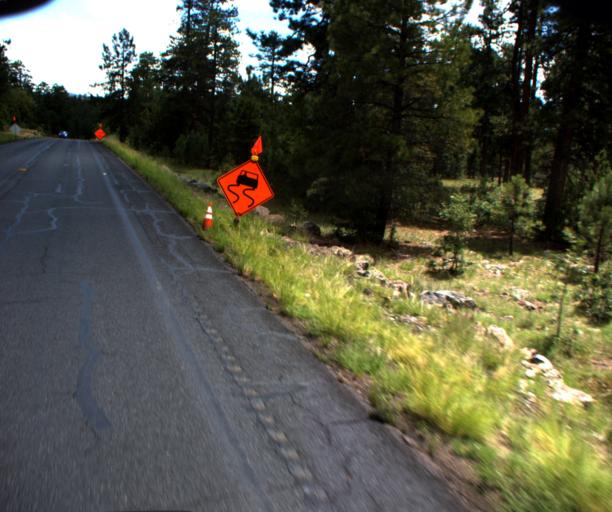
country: US
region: Arizona
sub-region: Gila County
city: Pine
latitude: 34.5015
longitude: -111.4643
